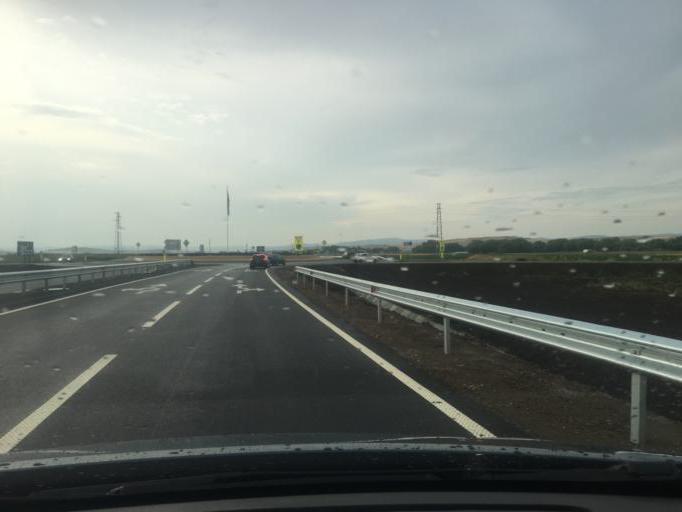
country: BG
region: Burgas
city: Aheloy
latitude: 42.6447
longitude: 27.6371
